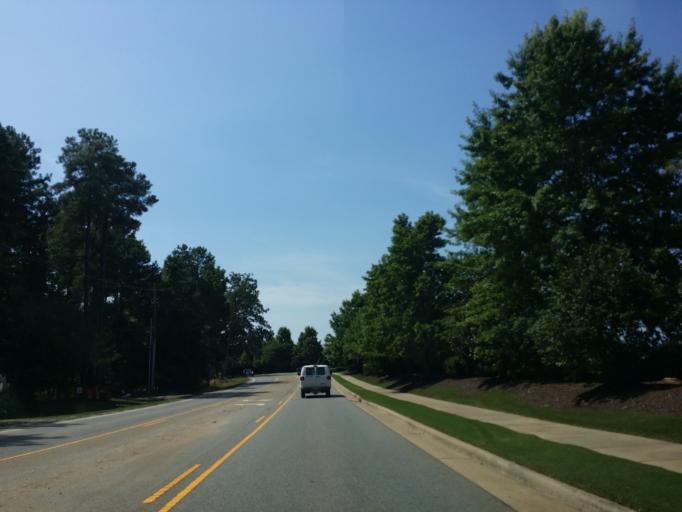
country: US
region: North Carolina
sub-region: Wake County
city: Cary
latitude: 35.8832
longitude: -78.7273
